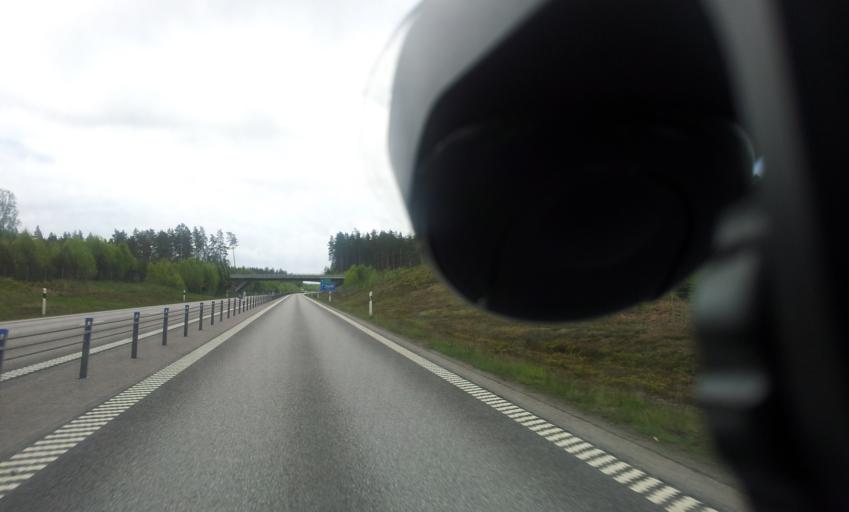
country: SE
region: Kalmar
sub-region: Torsas Kommun
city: Torsas
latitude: 56.5146
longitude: 16.0858
